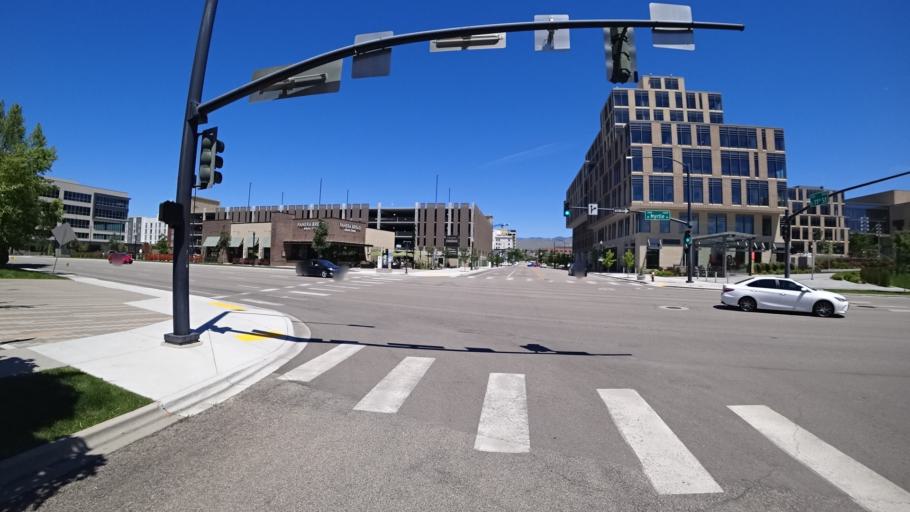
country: US
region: Idaho
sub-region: Ada County
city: Boise
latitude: 43.6148
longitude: -116.2096
